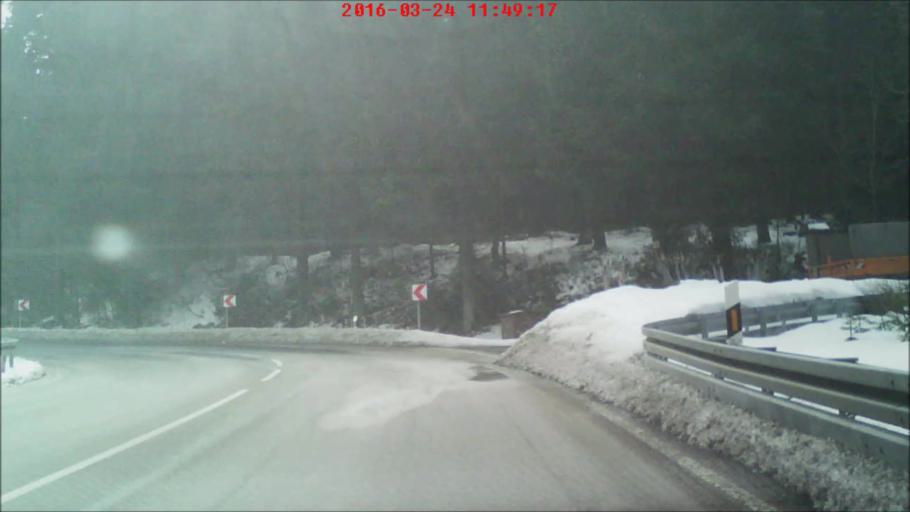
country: DE
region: Thuringia
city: Steinheid
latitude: 50.4654
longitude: 11.0348
